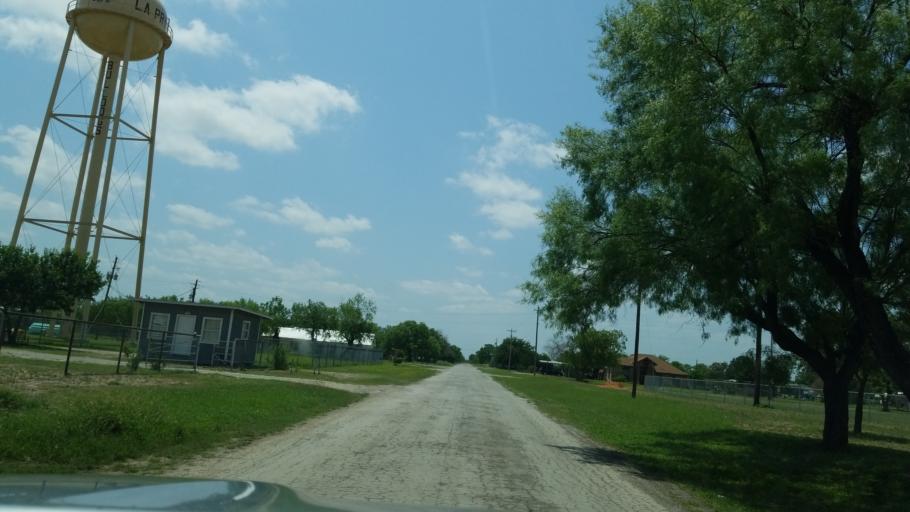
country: US
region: Texas
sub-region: Zavala County
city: La Pryor
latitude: 28.9437
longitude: -99.8420
